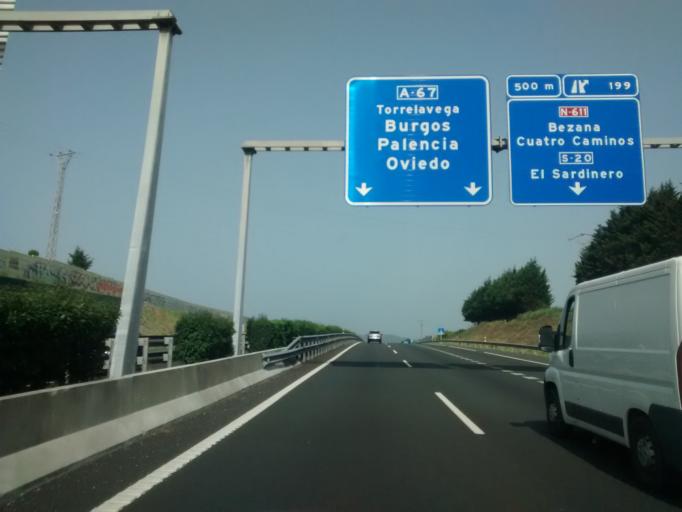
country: ES
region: Cantabria
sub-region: Provincia de Cantabria
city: Santa Cruz de Bezana
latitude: 43.4373
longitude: -3.8789
